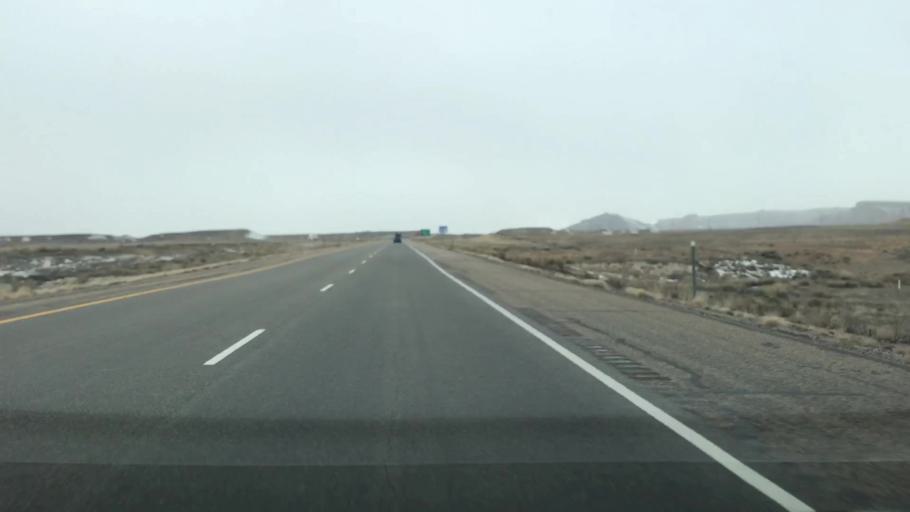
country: US
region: Utah
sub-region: Grand County
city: Moab
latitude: 38.9474
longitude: -109.7941
